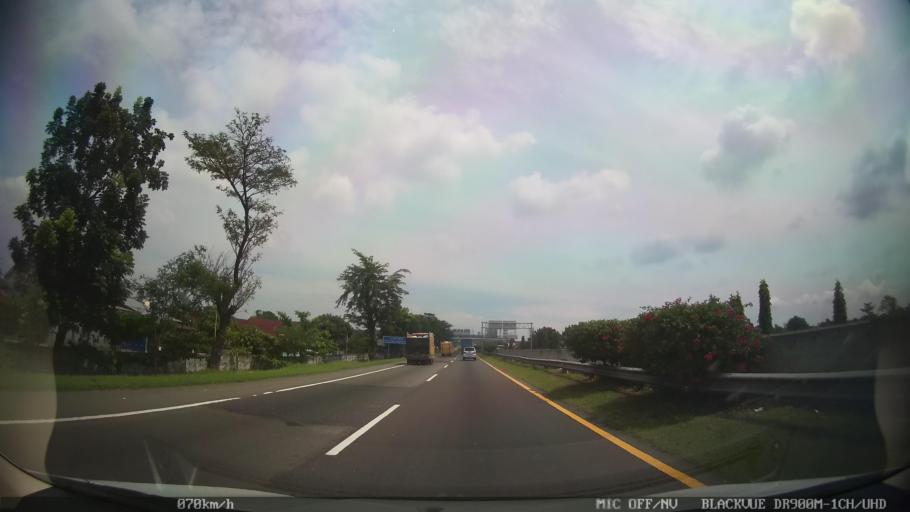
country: ID
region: North Sumatra
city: Labuhan Deli
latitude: 3.6553
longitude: 98.6826
